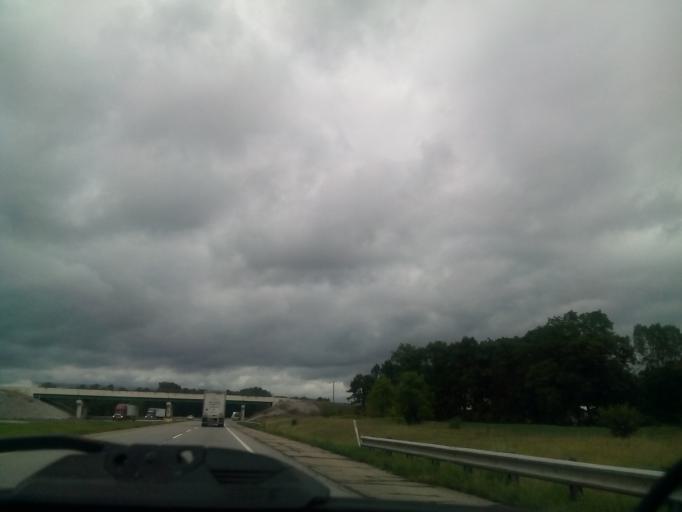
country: US
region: Michigan
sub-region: Branch County
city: Bronson
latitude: 41.7496
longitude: -85.2705
